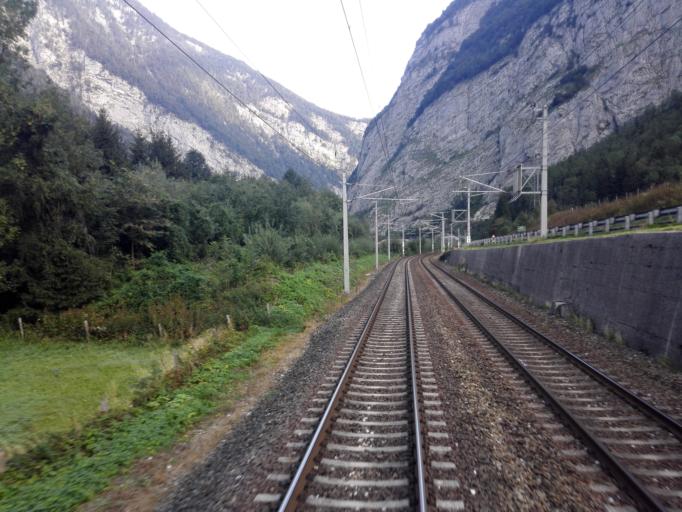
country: AT
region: Salzburg
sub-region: Politischer Bezirk Hallein
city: Golling an der Salzach
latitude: 47.5479
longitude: 13.1698
